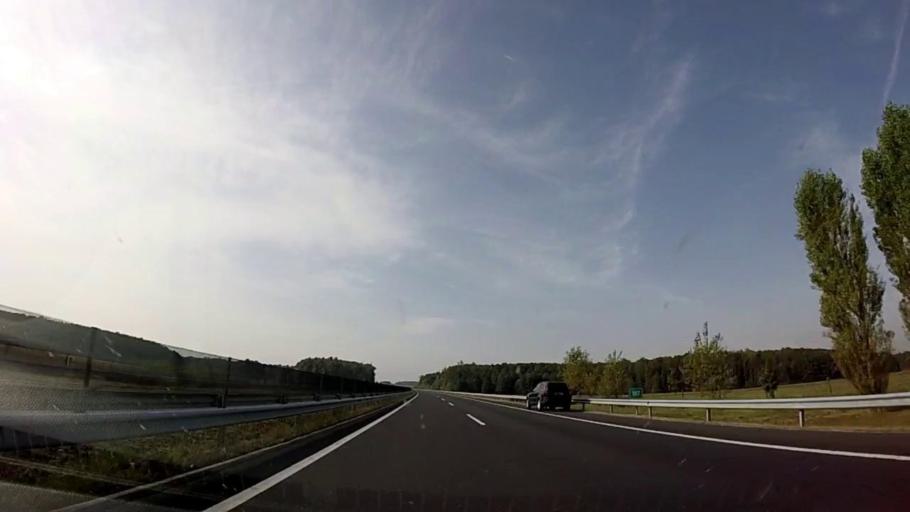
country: HU
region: Zala
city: Zalakomar
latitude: 46.5018
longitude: 17.1397
